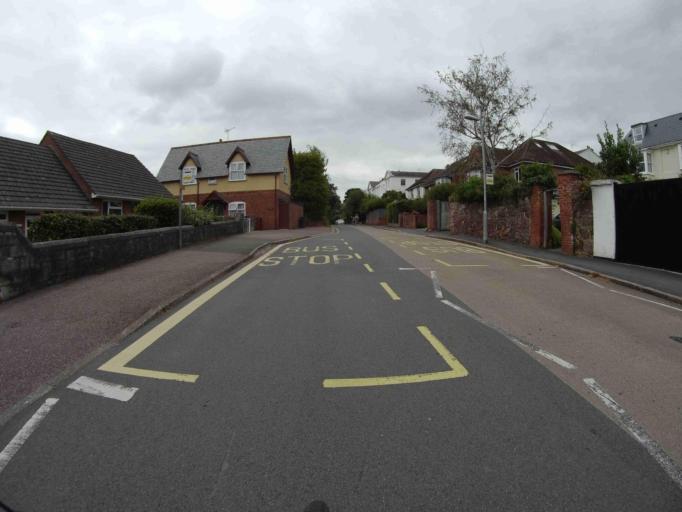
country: GB
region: England
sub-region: Devon
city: Exeter
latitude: 50.7181
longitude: -3.5179
